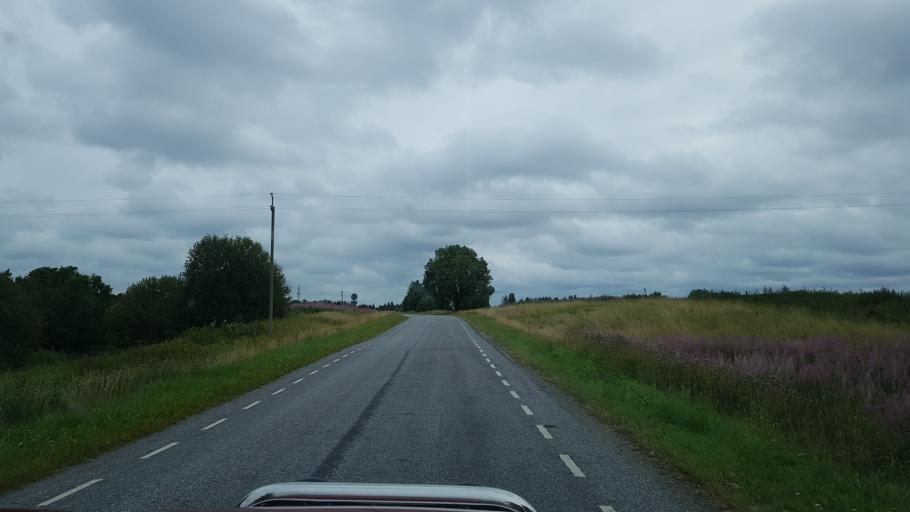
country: EE
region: Ida-Virumaa
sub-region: Puessi linn
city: Pussi
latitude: 59.3776
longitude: 27.0382
